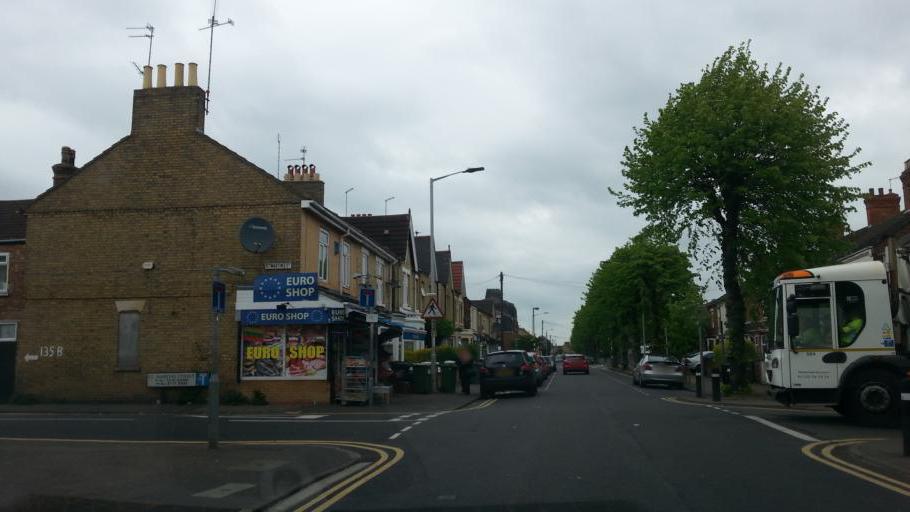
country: GB
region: England
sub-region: Peterborough
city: Peterborough
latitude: 52.5855
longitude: -0.2423
